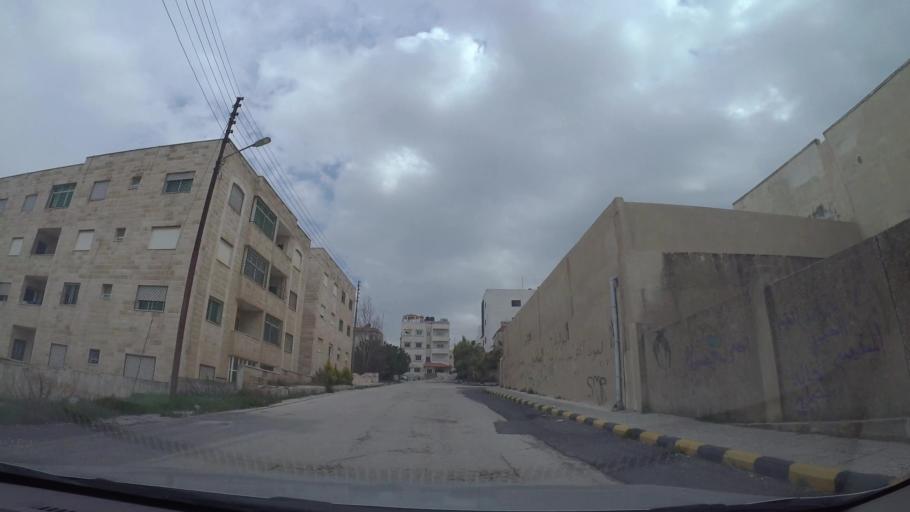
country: JO
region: Amman
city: Umm as Summaq
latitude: 31.8967
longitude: 35.8429
